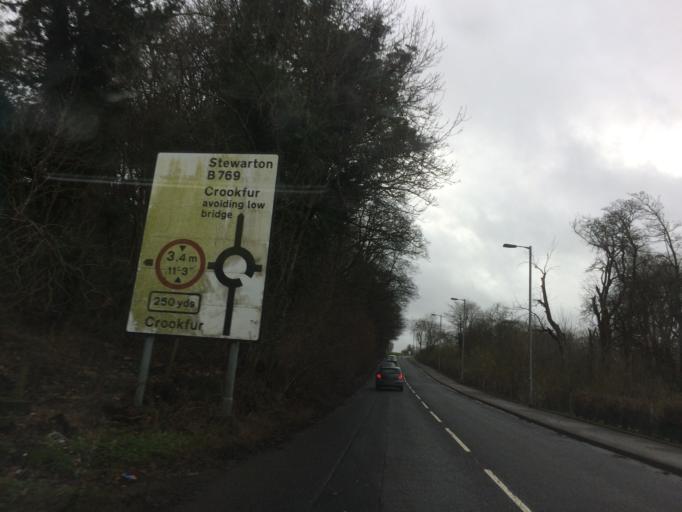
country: GB
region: Scotland
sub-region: East Renfrewshire
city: Newton Mearns
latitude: 55.7941
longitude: -4.3316
